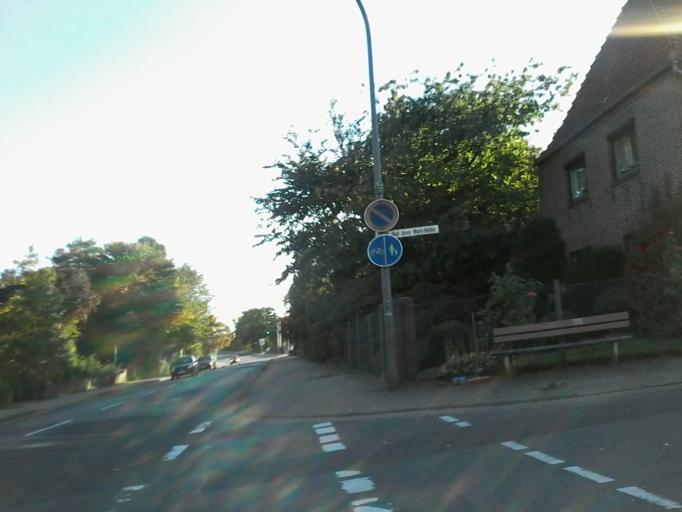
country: DE
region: Lower Saxony
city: Achim
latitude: 53.0188
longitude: 9.0313
